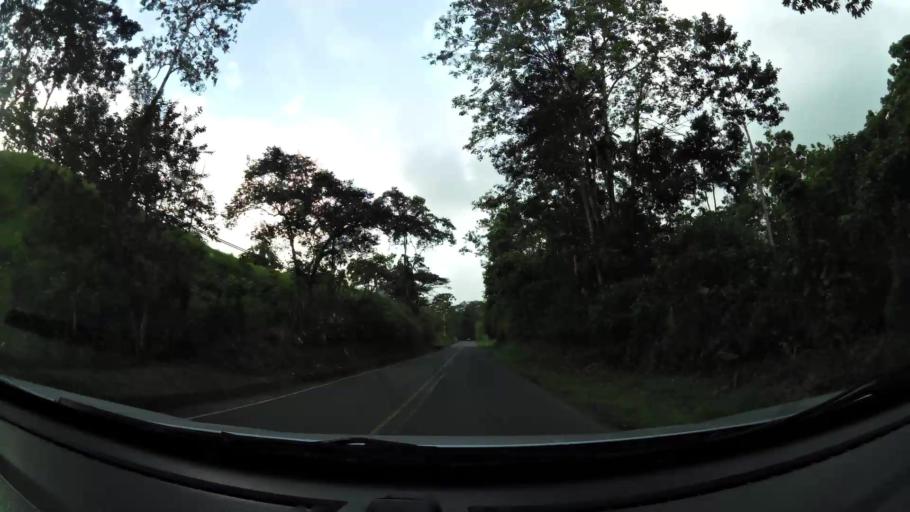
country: CR
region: Cartago
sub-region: Canton de Turrialba
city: La Suiza
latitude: 9.9768
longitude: -83.5695
